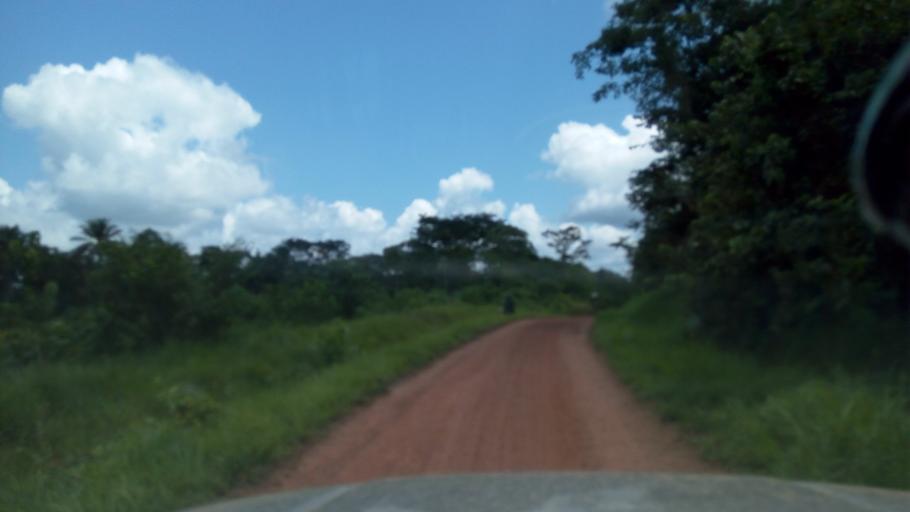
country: SL
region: Southern Province
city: Zimmi
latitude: 7.3082
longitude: -11.2999
